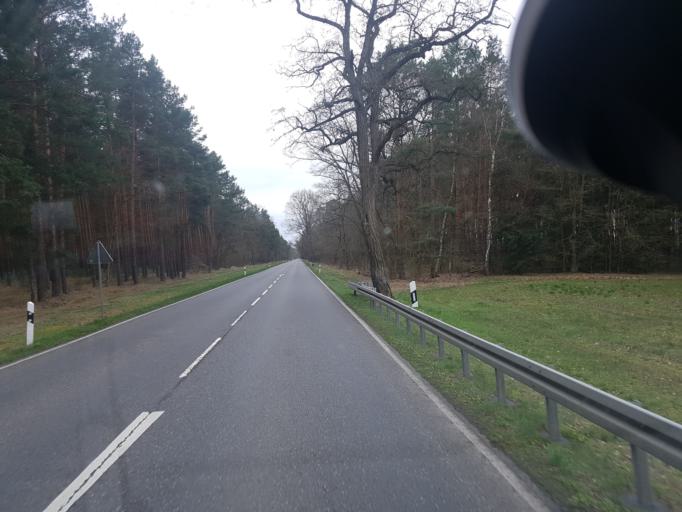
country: DE
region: Brandenburg
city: Schlepzig
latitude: 51.9813
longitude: 13.9635
